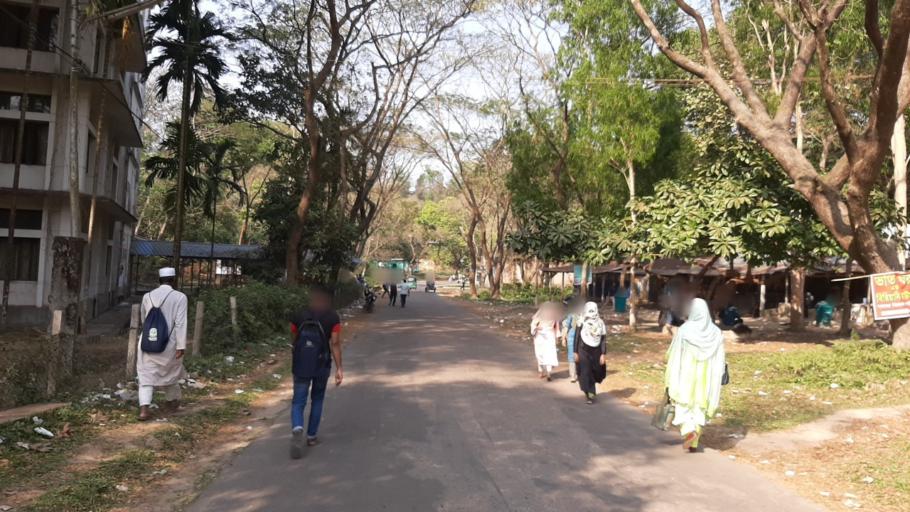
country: BD
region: Chittagong
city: Chittagong
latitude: 22.4733
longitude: 91.7882
